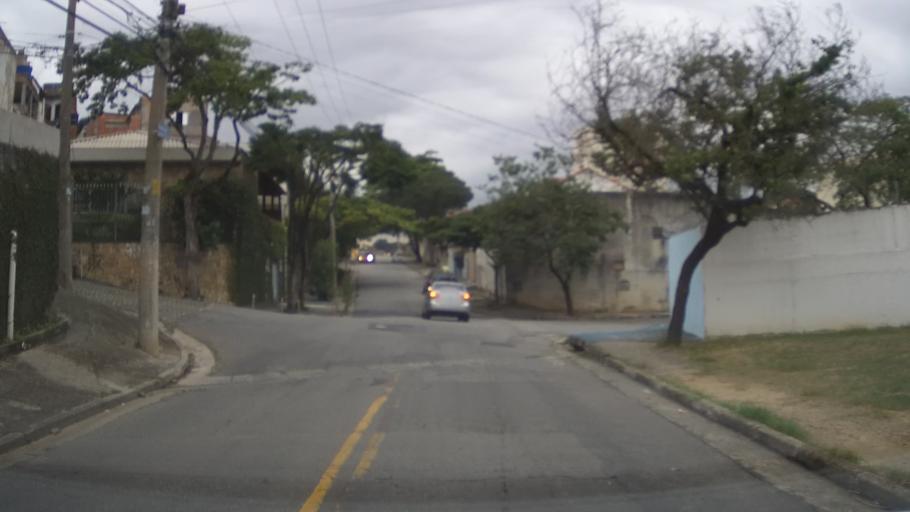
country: BR
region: Sao Paulo
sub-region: Guarulhos
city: Guarulhos
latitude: -23.4576
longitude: -46.5560
